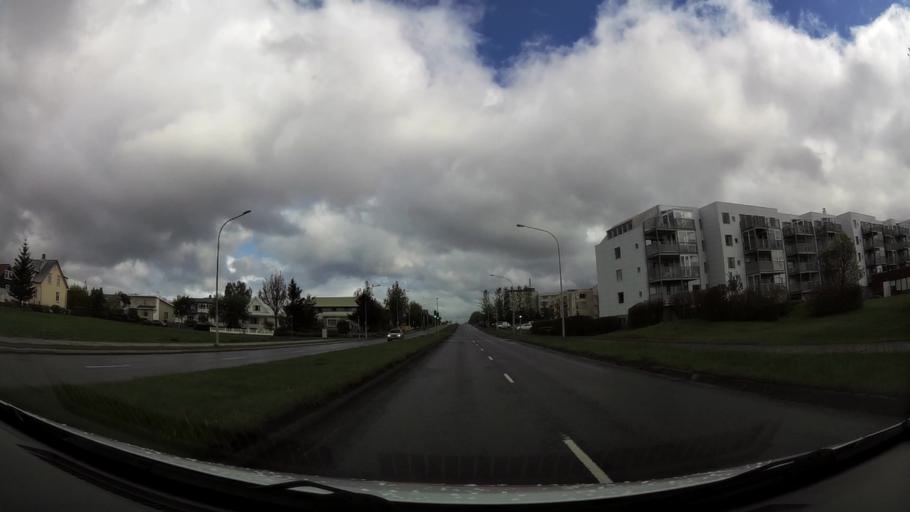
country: IS
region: Capital Region
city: Seltjarnarnes
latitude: 64.1344
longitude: -21.9576
